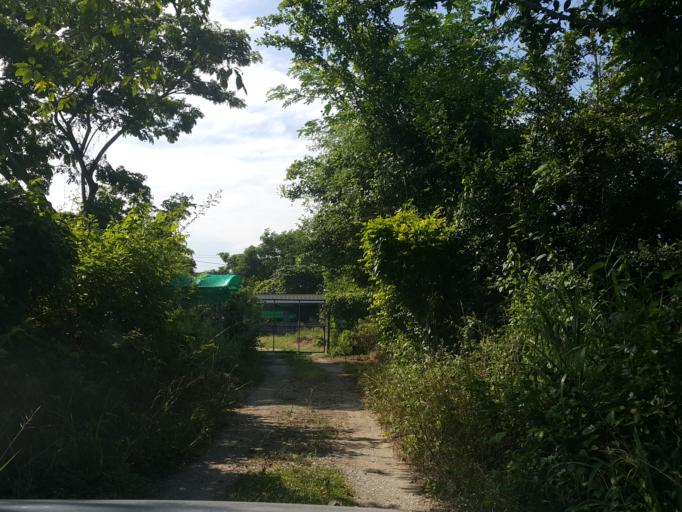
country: TH
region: Chiang Mai
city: Saraphi
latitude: 18.7308
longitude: 99.0452
